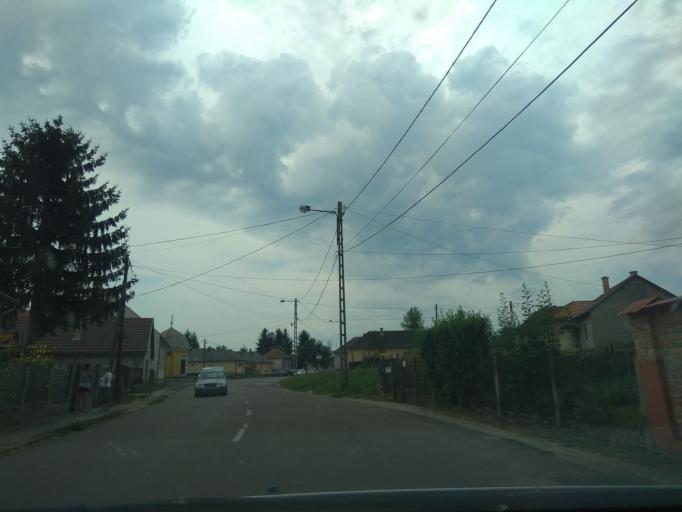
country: HU
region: Heves
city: Petervasara
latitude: 48.0220
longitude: 20.1019
